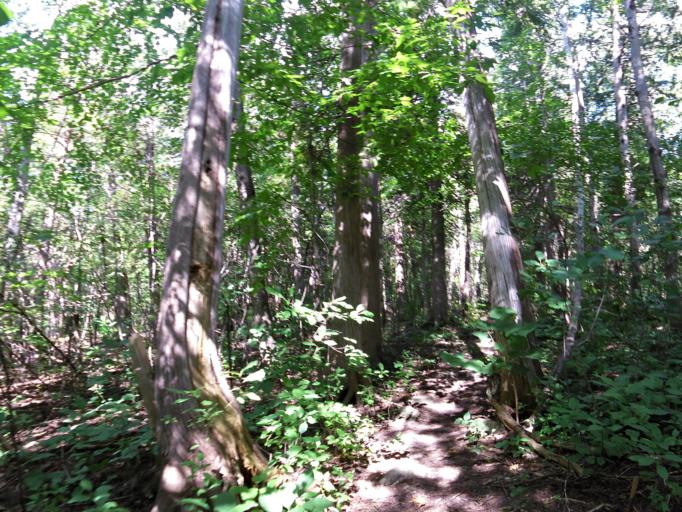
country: CA
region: Ontario
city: Ottawa
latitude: 45.3704
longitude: -75.7412
